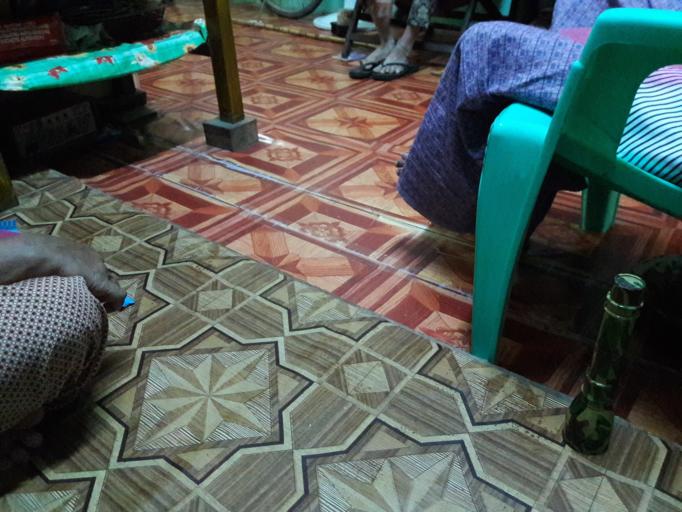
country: MM
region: Yangon
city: Yangon
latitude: 16.9365
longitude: 96.1891
